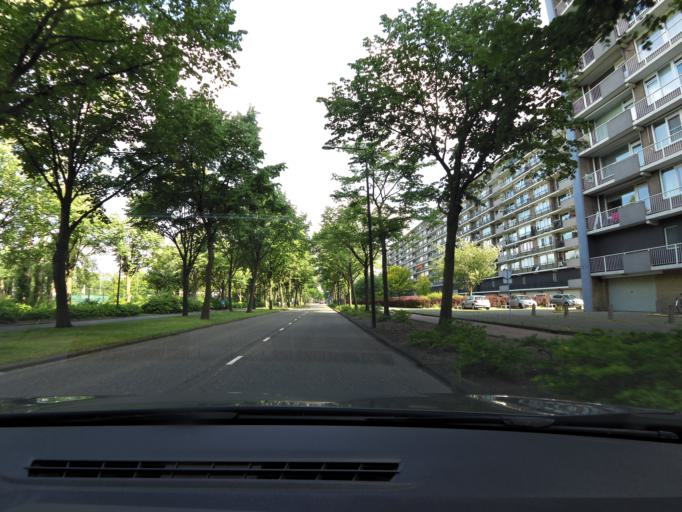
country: NL
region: South Holland
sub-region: Gemeente Vlaardingen
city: Vlaardingen
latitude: 51.9257
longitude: 4.3452
